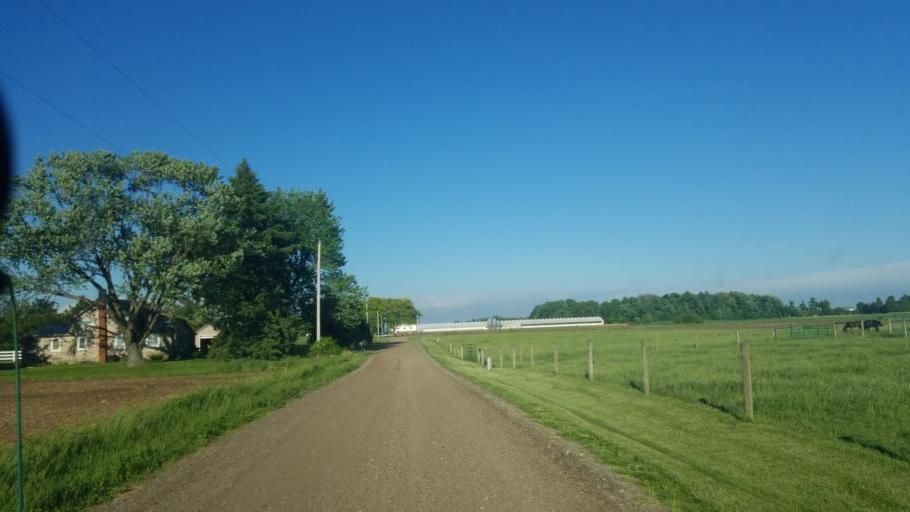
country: US
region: Indiana
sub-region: Marshall County
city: Bremen
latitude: 41.4098
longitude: -86.1007
